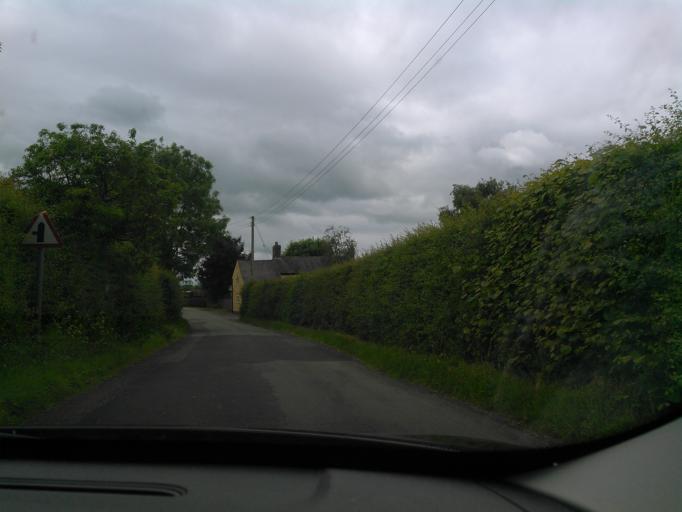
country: GB
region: England
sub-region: Shropshire
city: Wem
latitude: 52.9188
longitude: -2.7272
